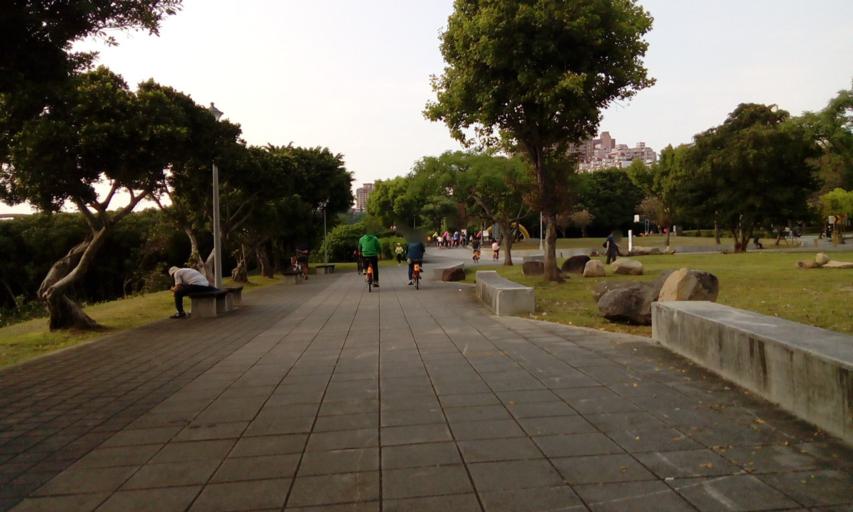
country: TW
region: Taipei
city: Taipei
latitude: 25.1223
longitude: 121.4617
